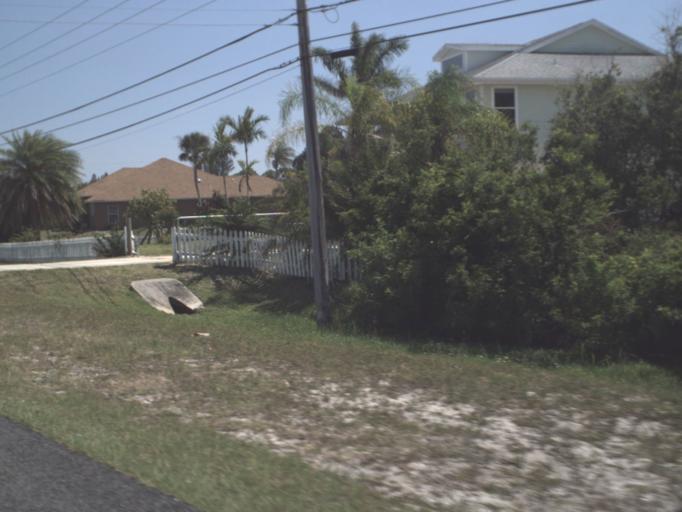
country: US
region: Florida
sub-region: Brevard County
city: Grant-Valkaria
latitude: 27.9622
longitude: -80.5408
